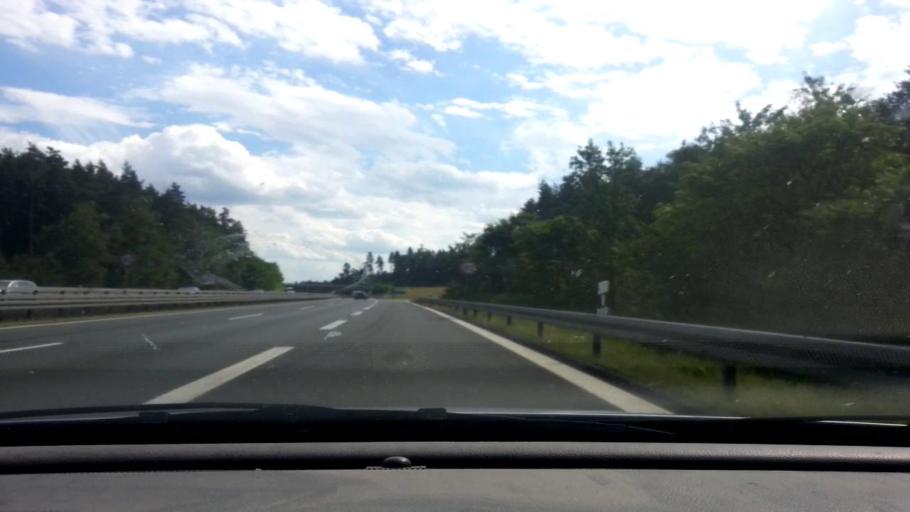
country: DE
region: Bavaria
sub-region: Upper Palatinate
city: Wiesau
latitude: 49.8618
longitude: 12.1808
